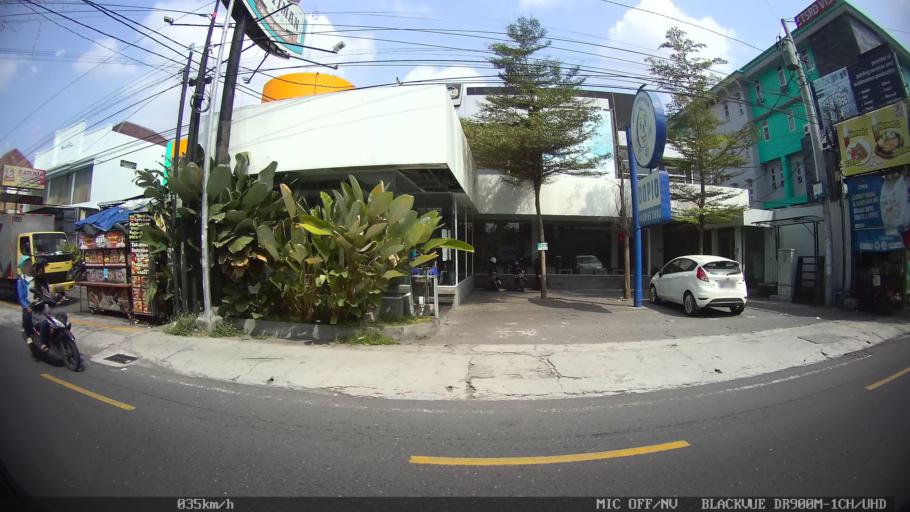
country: ID
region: Daerah Istimewa Yogyakarta
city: Yogyakarta
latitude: -7.8137
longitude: 110.3764
